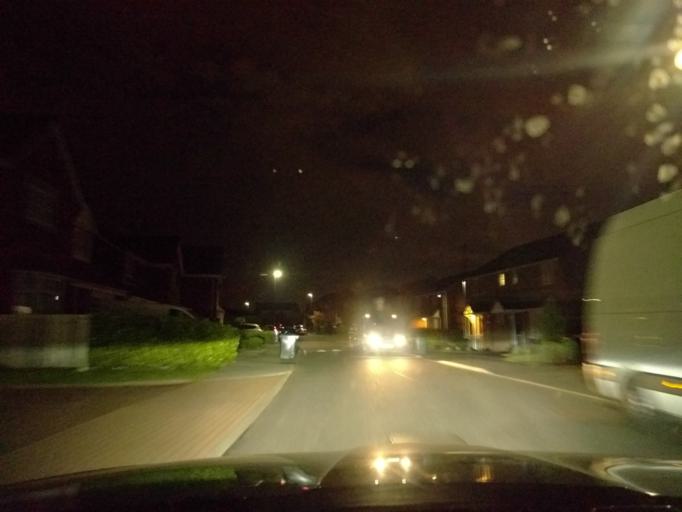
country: GB
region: England
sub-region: Northumberland
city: Backworth
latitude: 55.0234
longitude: -1.5316
